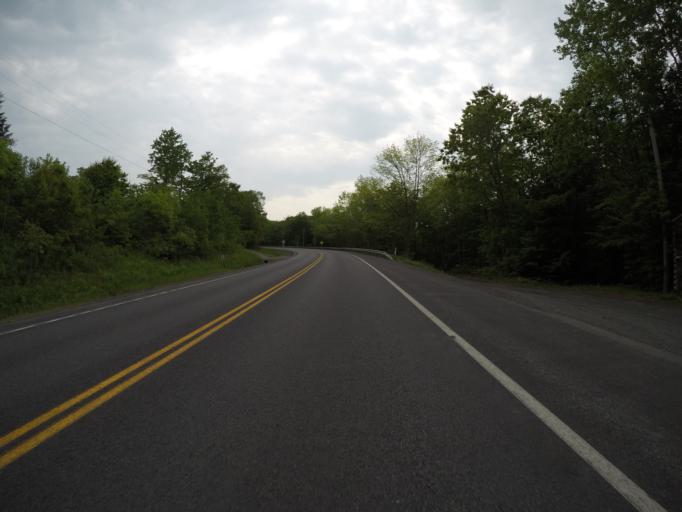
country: US
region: New York
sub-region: Sullivan County
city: Livingston Manor
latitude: 42.0606
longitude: -74.9312
